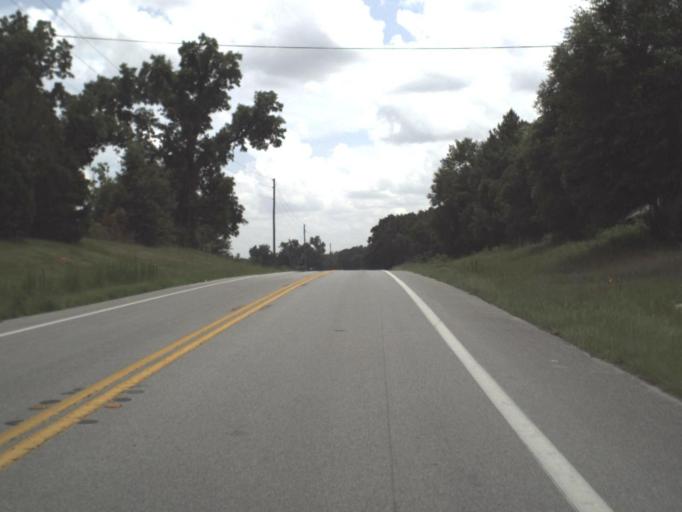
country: US
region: Florida
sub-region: Madison County
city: Madison
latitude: 30.5118
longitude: -83.4228
